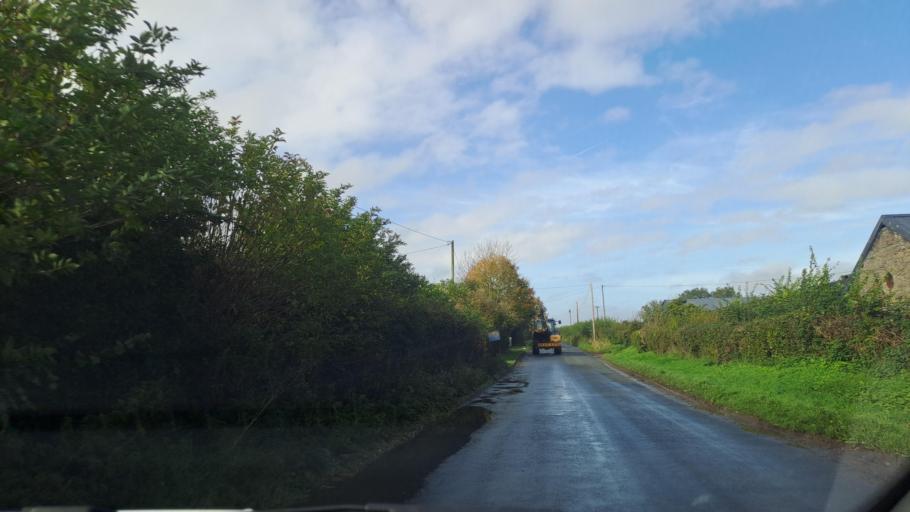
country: IE
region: Ulster
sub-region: County Monaghan
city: Carrickmacross
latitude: 53.8689
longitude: -6.6629
